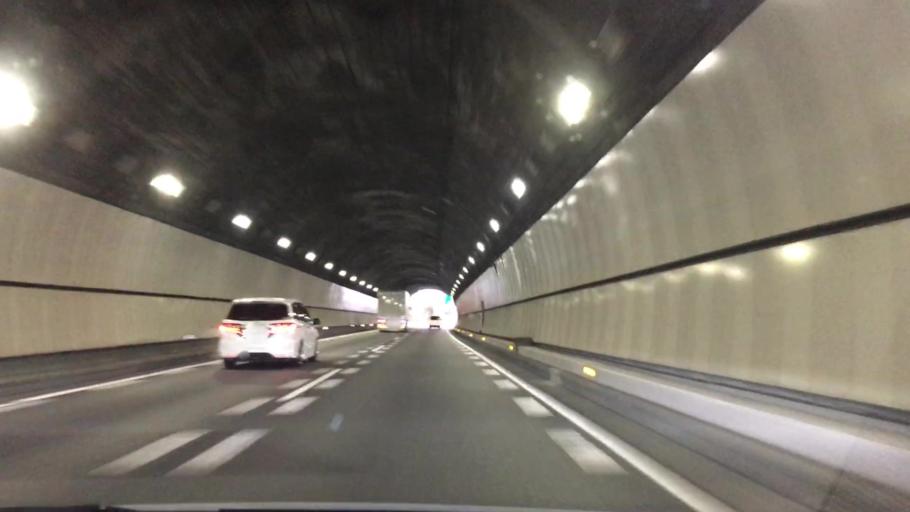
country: JP
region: Shizuoka
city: Shizuoka-shi
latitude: 35.0497
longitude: 138.4993
